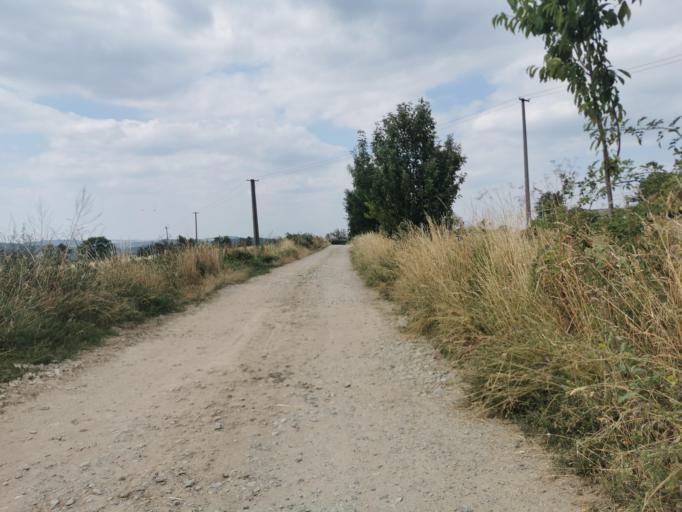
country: SK
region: Nitriansky
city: Brezova pod Bradlom
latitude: 48.6983
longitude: 17.5035
